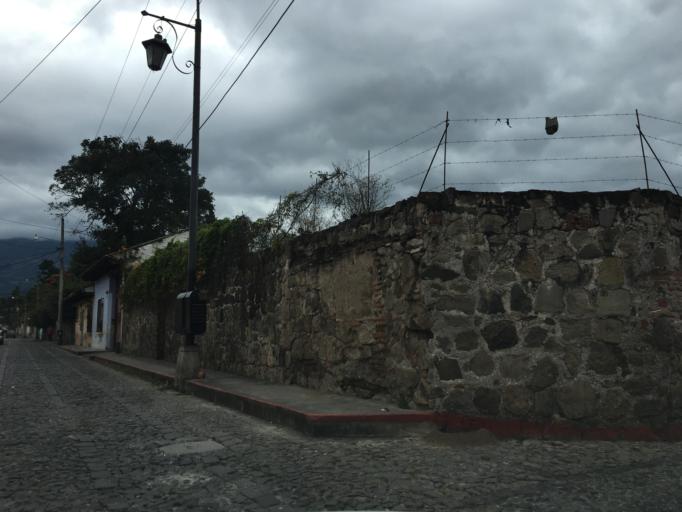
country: GT
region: Sacatepequez
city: Antigua Guatemala
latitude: 14.5515
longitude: -90.7311
